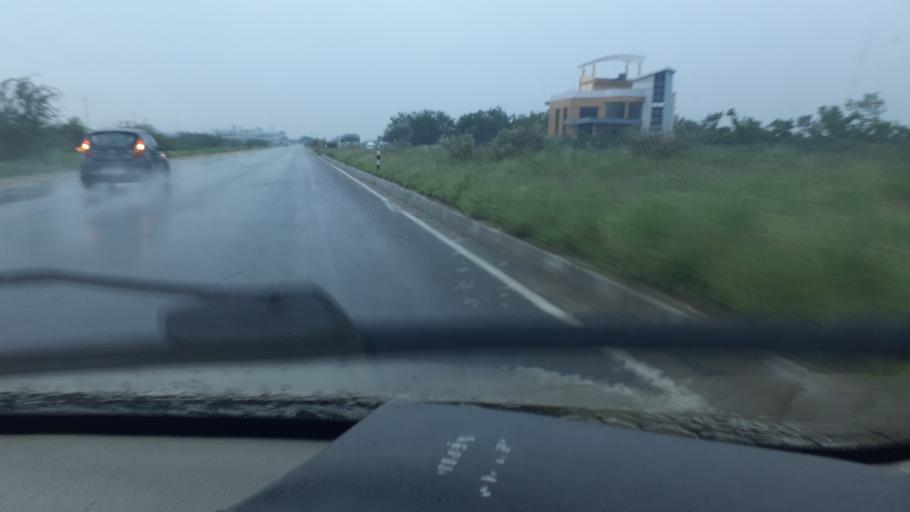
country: IN
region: Tamil Nadu
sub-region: Virudhunagar
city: Sattur
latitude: 9.4063
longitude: 77.9160
